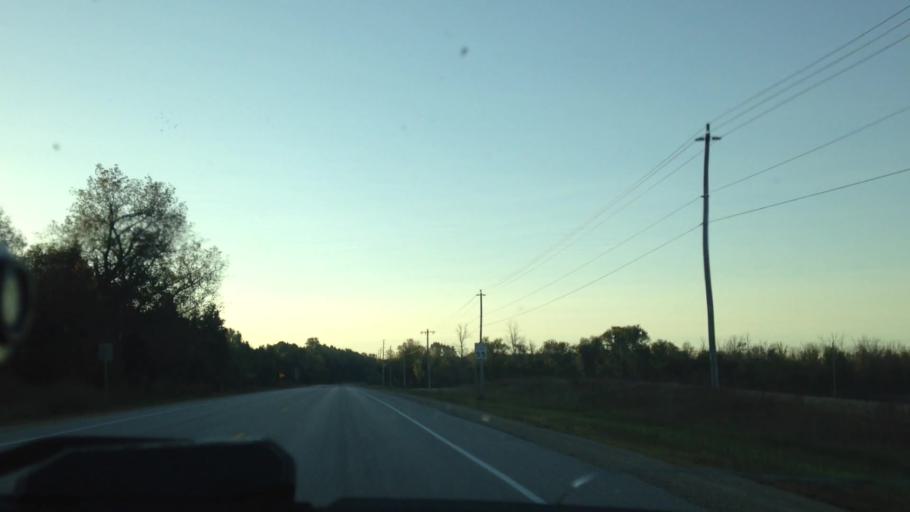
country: US
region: Wisconsin
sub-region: Washington County
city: Newburg
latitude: 43.4270
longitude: -88.0372
